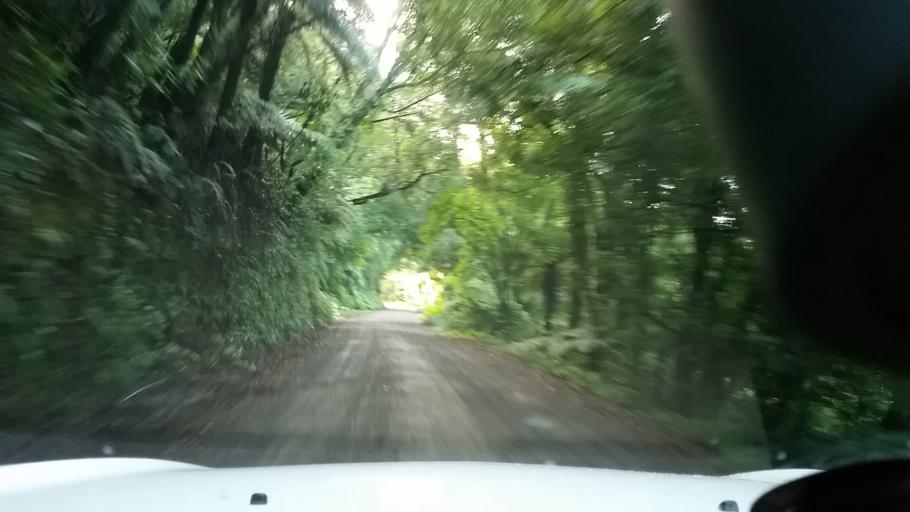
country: NZ
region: Bay of Plenty
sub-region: Kawerau District
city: Kawerau
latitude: -38.0189
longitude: 176.5959
